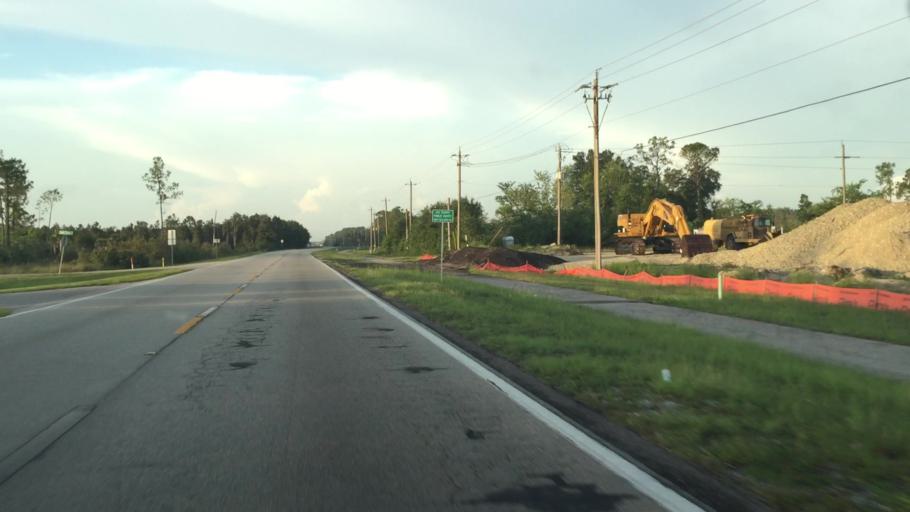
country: US
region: Florida
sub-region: Lee County
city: Fort Myers
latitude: 26.6301
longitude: -81.8115
